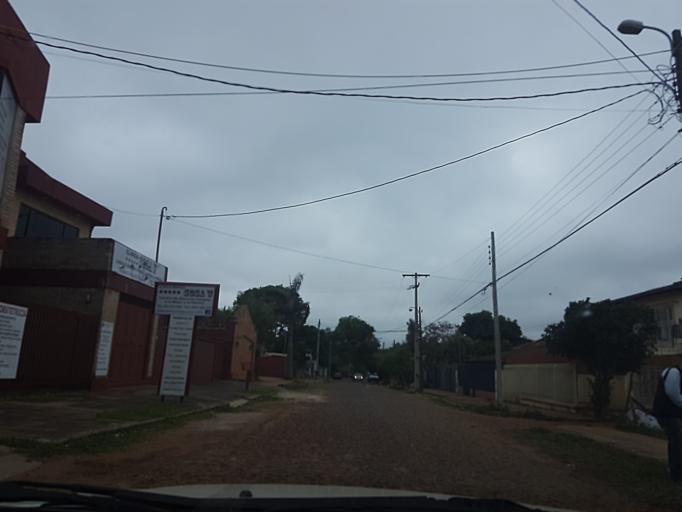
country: PY
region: Central
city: Fernando de la Mora
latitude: -25.3411
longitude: -57.5366
